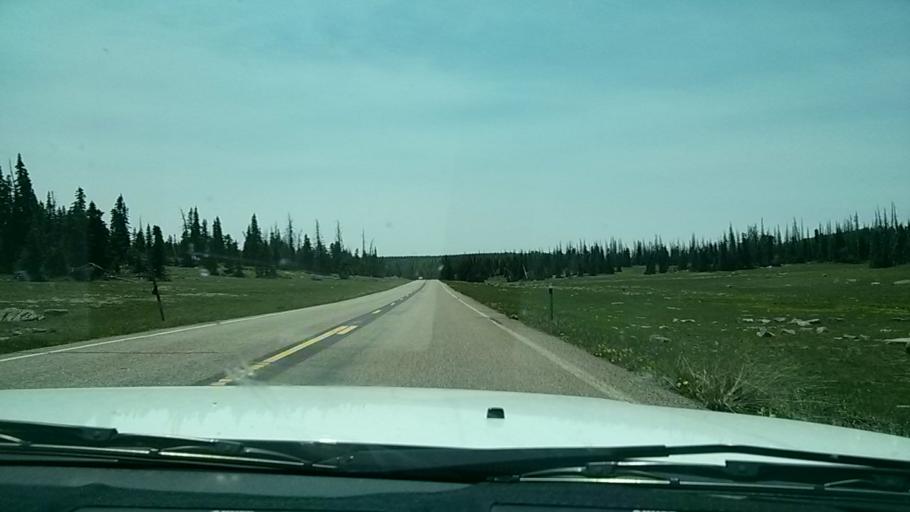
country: US
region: Utah
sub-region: Iron County
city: Cedar City
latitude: 37.5933
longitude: -112.8494
